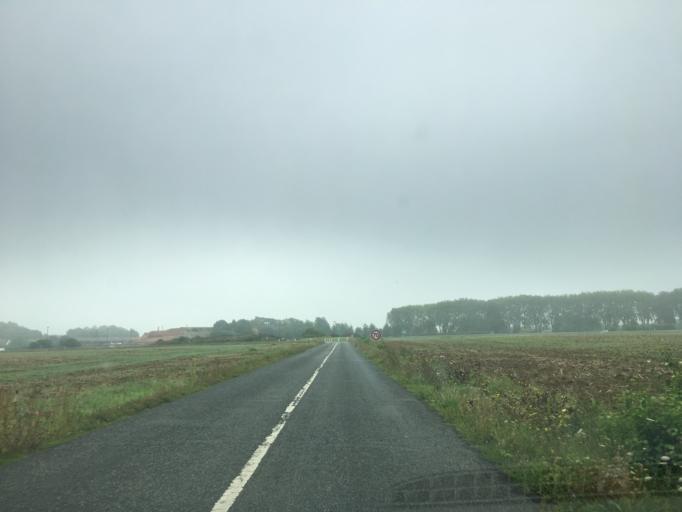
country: FR
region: Ile-de-France
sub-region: Departement de l'Essonne
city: Tigery
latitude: 48.6374
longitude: 2.4971
